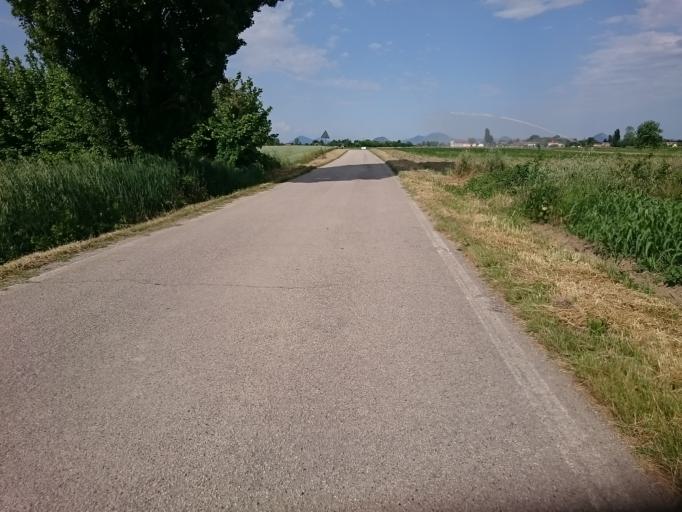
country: IT
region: Veneto
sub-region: Provincia di Padova
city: Casale di Scodosia
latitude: 45.2062
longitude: 11.4850
